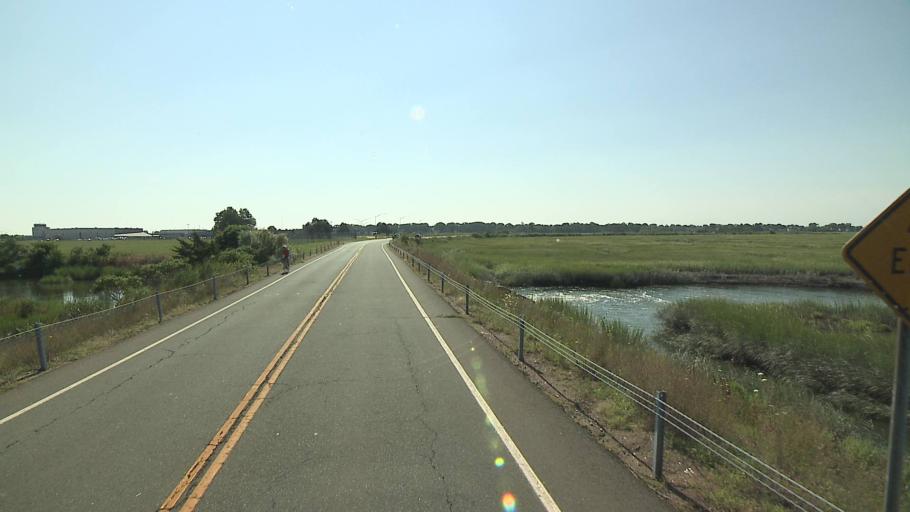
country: US
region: Connecticut
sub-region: Fairfield County
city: Stratford
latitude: 41.1631
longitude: -73.1358
